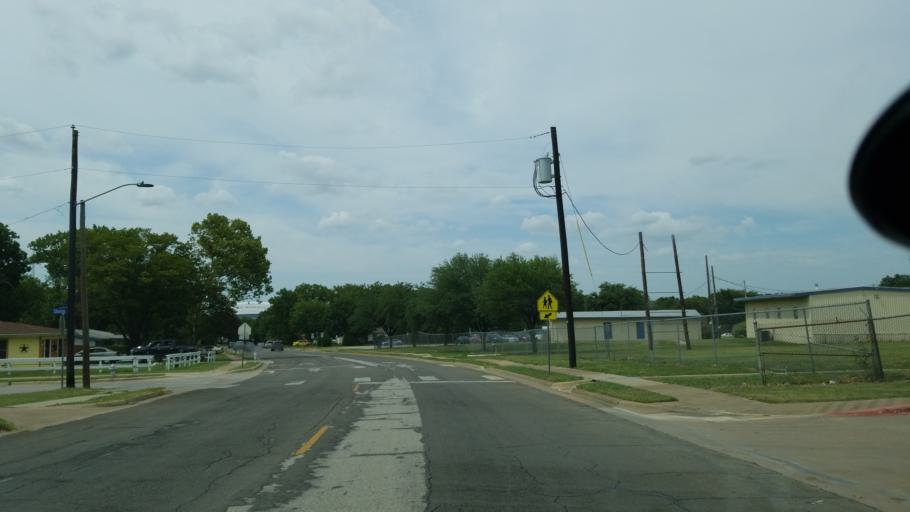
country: US
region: Texas
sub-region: Tarrant County
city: Arlington
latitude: 32.7302
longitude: -97.0830
